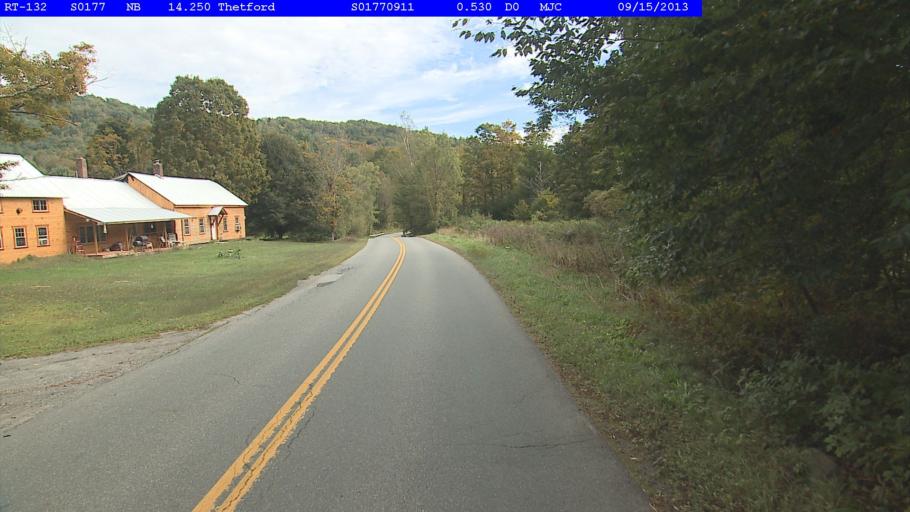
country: US
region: New Hampshire
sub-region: Grafton County
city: Hanover
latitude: 43.8330
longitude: -72.3115
